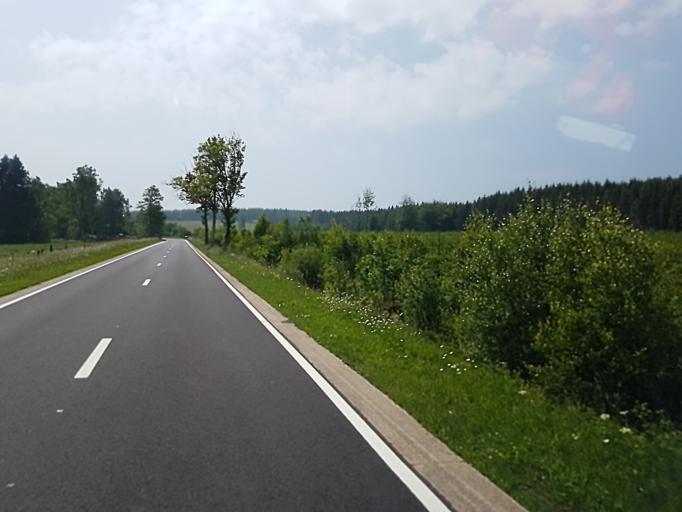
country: BE
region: Wallonia
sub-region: Province de Liege
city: Lierneux
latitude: 50.3389
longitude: 5.7909
